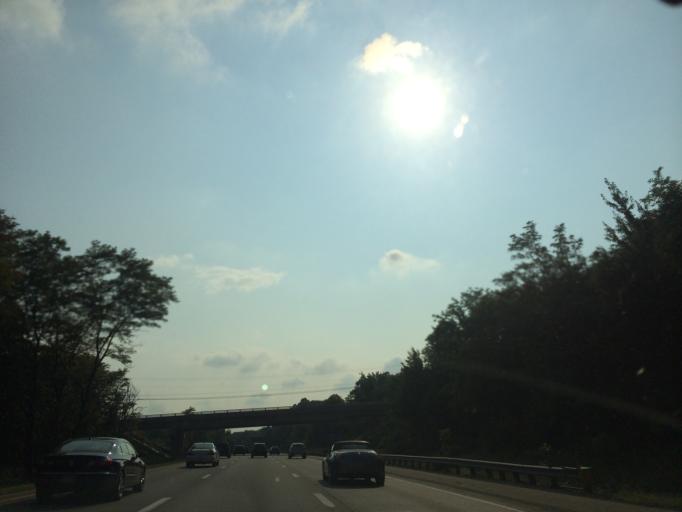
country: US
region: Pennsylvania
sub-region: Cumberland County
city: Enola
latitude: 40.3067
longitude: -76.9548
